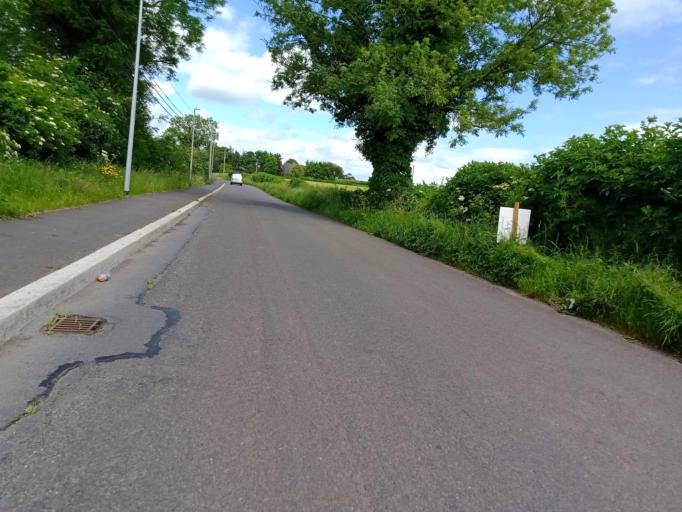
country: IE
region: Leinster
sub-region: Kilkenny
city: Kilkenny
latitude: 52.6801
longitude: -7.2490
